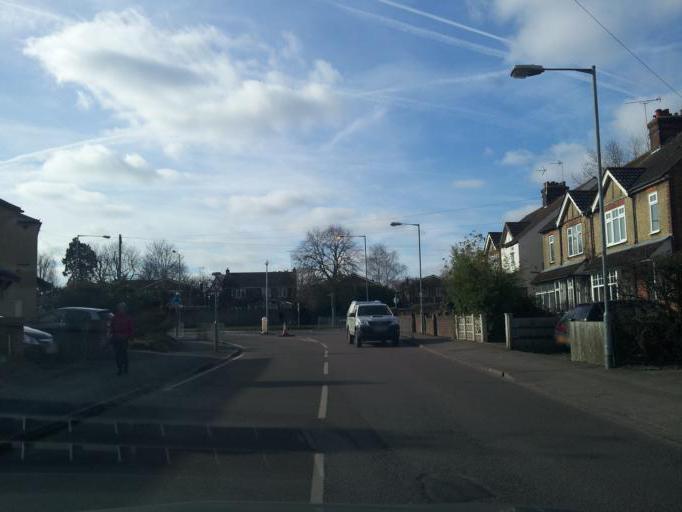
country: GB
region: England
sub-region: Hertfordshire
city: St Albans
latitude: 51.7474
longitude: -0.3152
